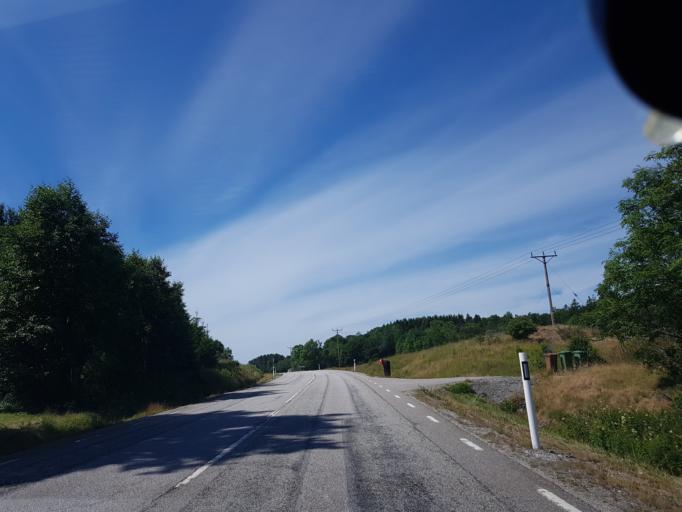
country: SE
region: Vaestra Goetaland
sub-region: Lysekils Kommun
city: Lysekil
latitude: 58.1651
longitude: 11.4797
